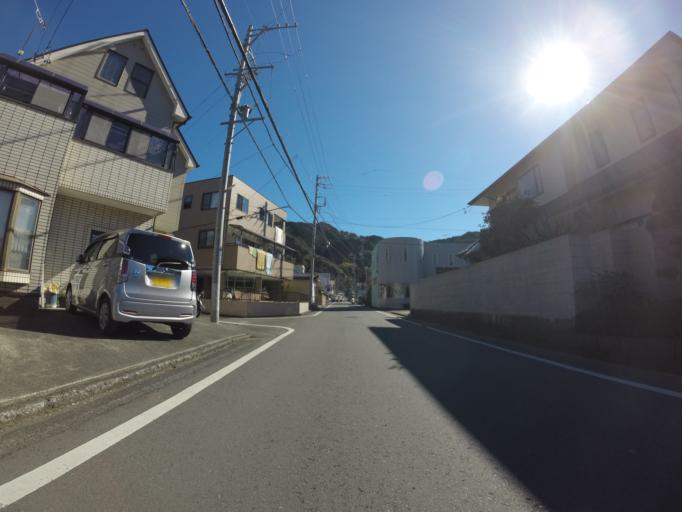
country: JP
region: Shizuoka
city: Shizuoka-shi
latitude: 35.0381
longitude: 138.3978
